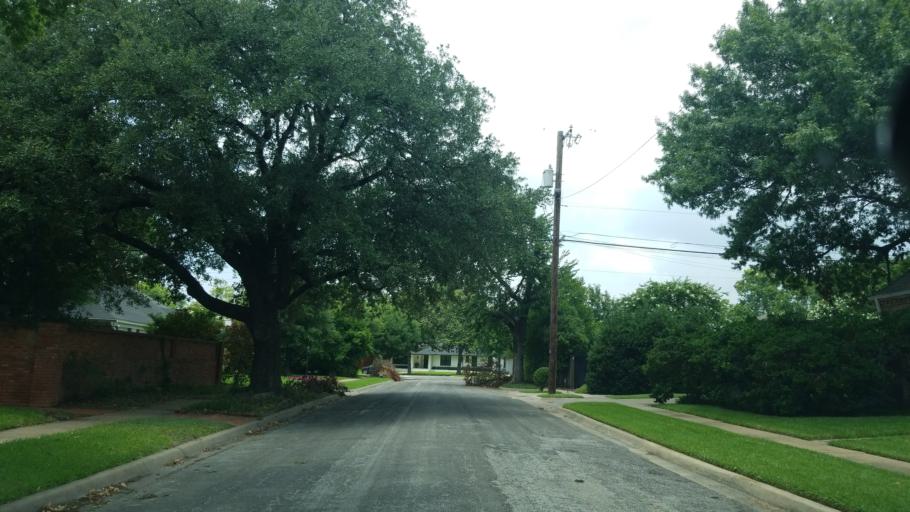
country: US
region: Texas
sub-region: Dallas County
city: University Park
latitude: 32.8338
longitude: -96.8215
